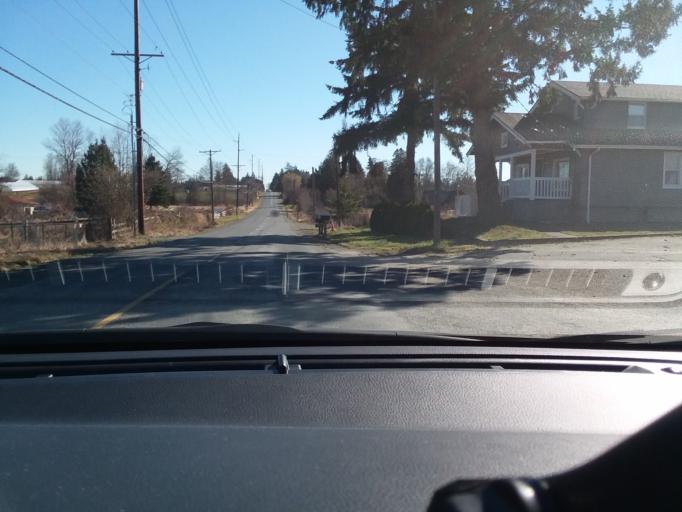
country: US
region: Washington
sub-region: Pierce County
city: Midland
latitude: 47.1700
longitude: -122.3948
